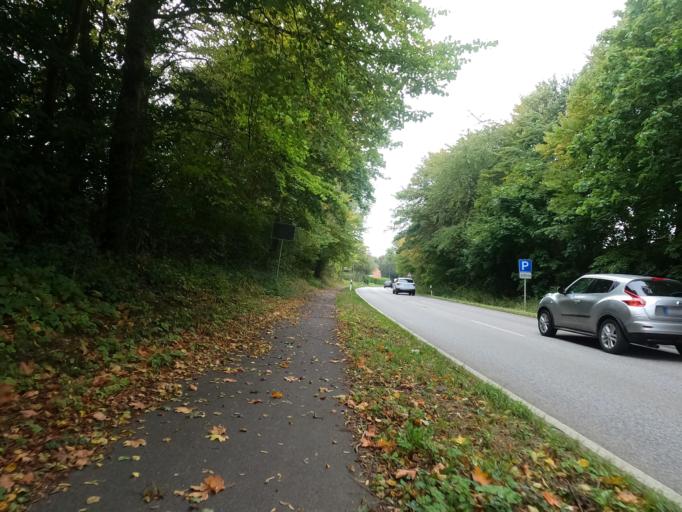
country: DE
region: Schleswig-Holstein
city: Heiligenhafen
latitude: 54.3536
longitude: 11.0116
